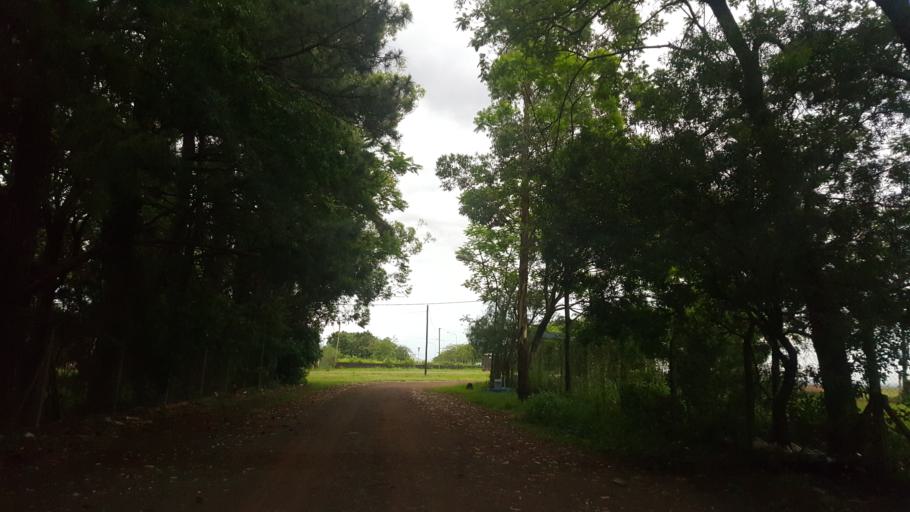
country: AR
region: Misiones
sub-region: Departamento de Capital
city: Posadas
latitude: -27.3982
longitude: -55.9733
